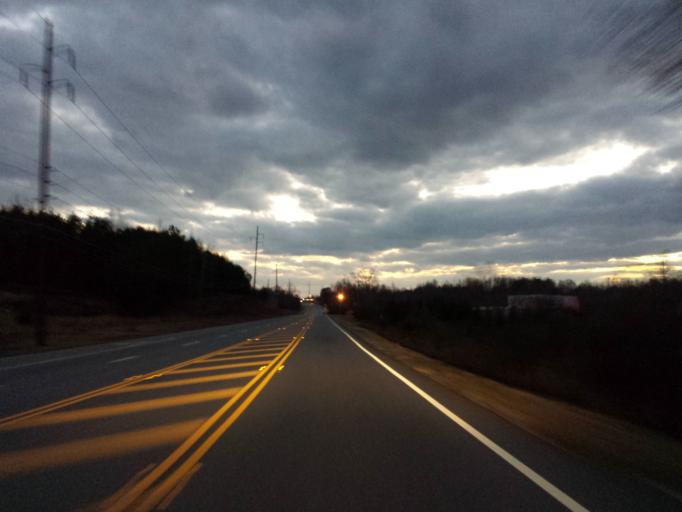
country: US
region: Georgia
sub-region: White County
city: Cleveland
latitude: 34.6347
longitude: -83.7468
